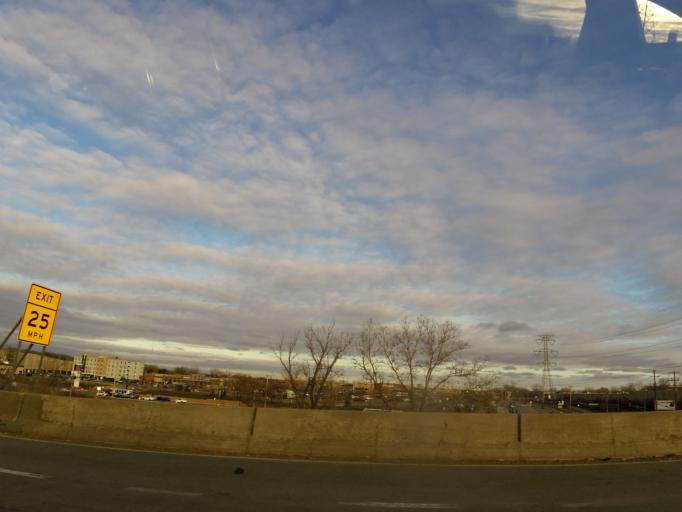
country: US
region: Minnesota
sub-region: Ramsey County
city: Lauderdale
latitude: 45.0207
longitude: -93.1892
